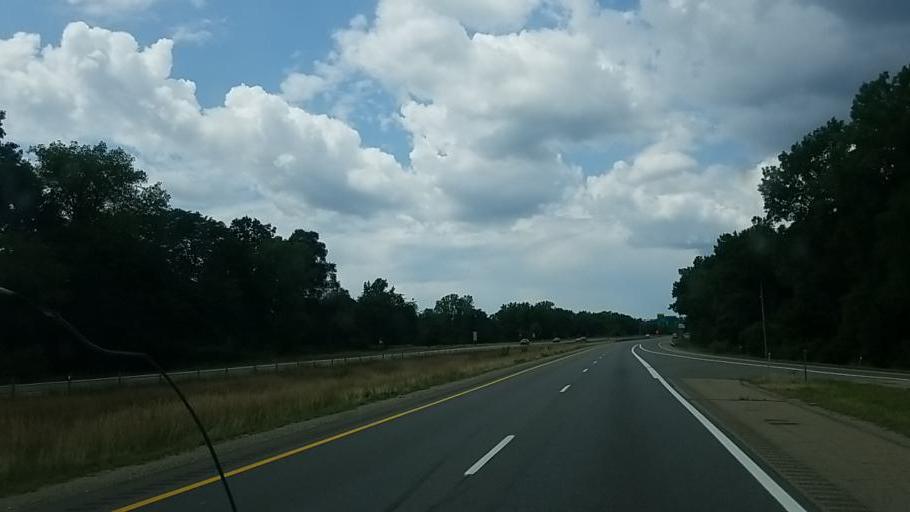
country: US
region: Michigan
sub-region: Kent County
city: East Grand Rapids
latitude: 42.9643
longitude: -85.5806
